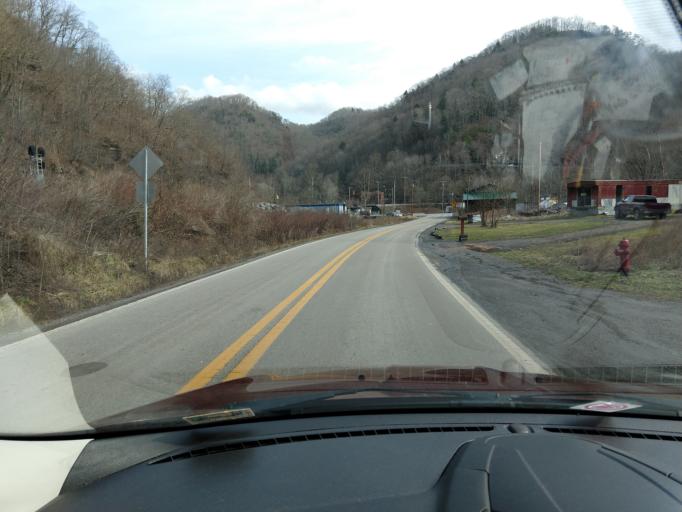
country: US
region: West Virginia
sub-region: McDowell County
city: Welch
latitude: 37.3215
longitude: -81.6985
